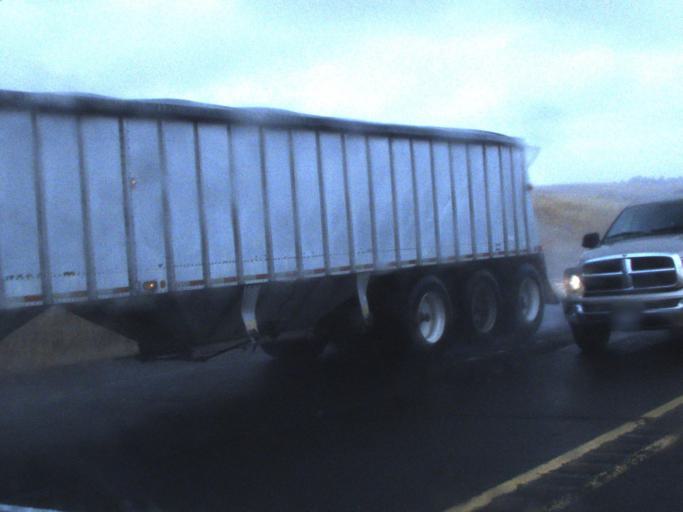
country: US
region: Washington
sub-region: Whitman County
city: Colfax
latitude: 47.2054
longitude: -117.3647
